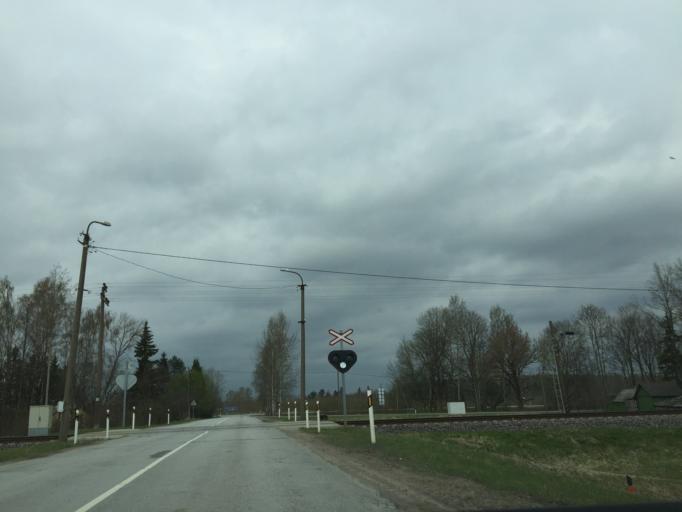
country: EE
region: Tartu
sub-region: Noo vald
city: Noo
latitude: 58.2798
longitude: 26.5279
